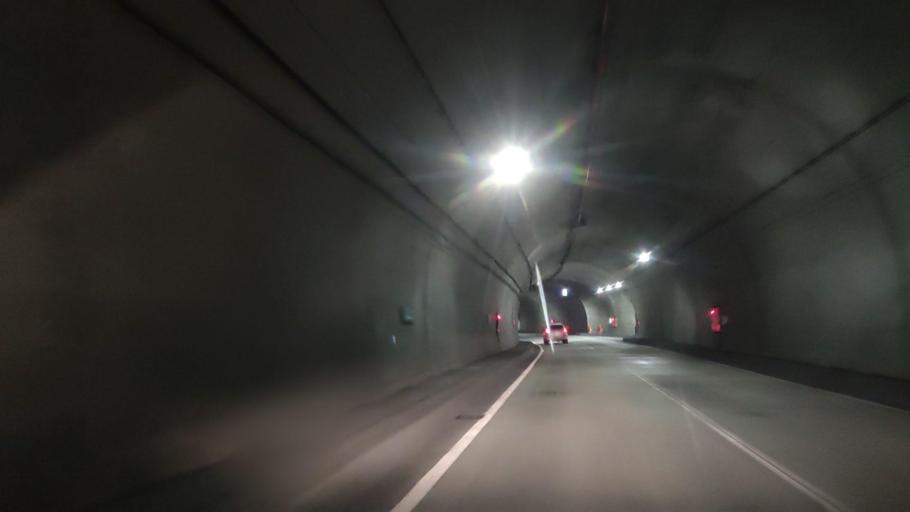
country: JP
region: Hokkaido
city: Rumoi
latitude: 43.7127
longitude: 141.3311
